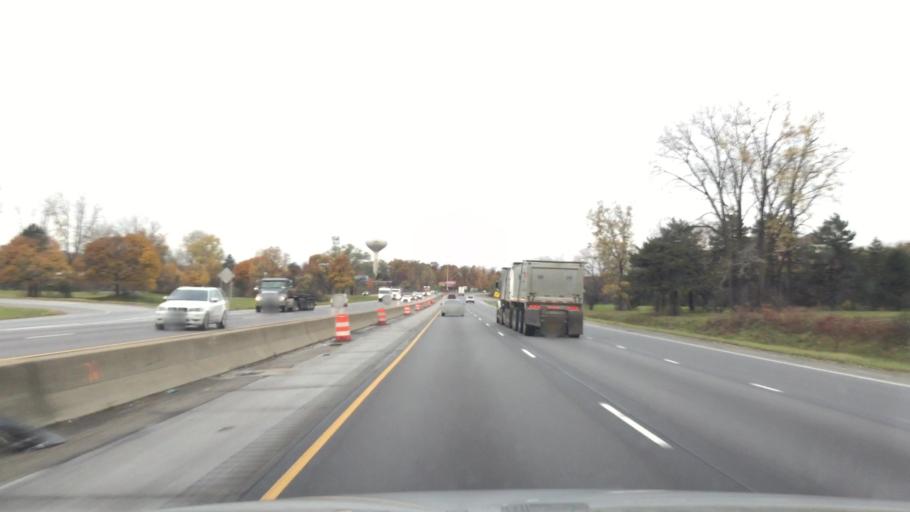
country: US
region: Michigan
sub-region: Washtenaw County
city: Ann Arbor
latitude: 42.2370
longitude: -83.7394
